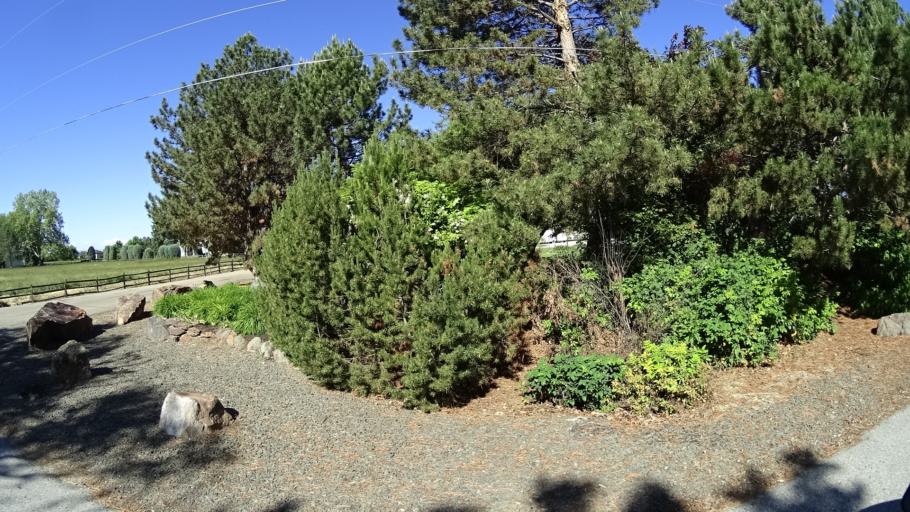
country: US
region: Idaho
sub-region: Ada County
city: Eagle
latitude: 43.6727
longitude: -116.3935
